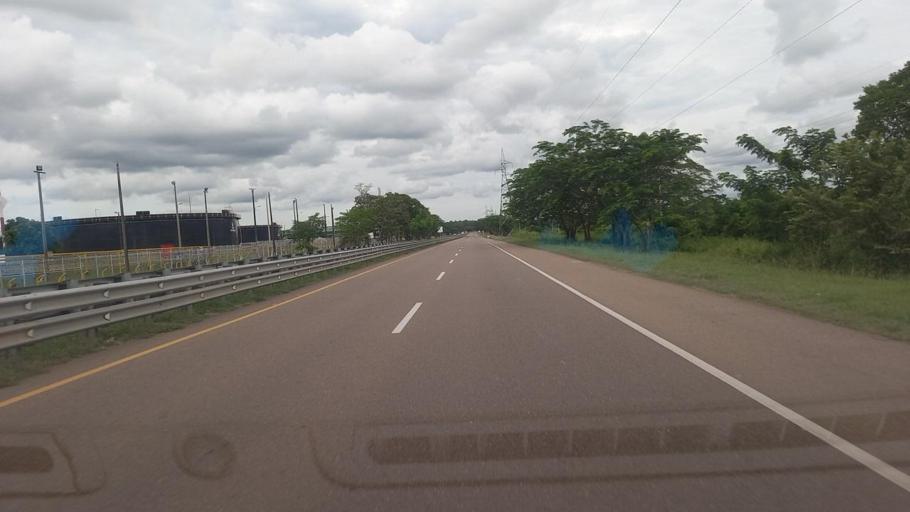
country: CO
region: Boyaca
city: Puerto Boyaca
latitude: 6.0614
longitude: -74.5590
